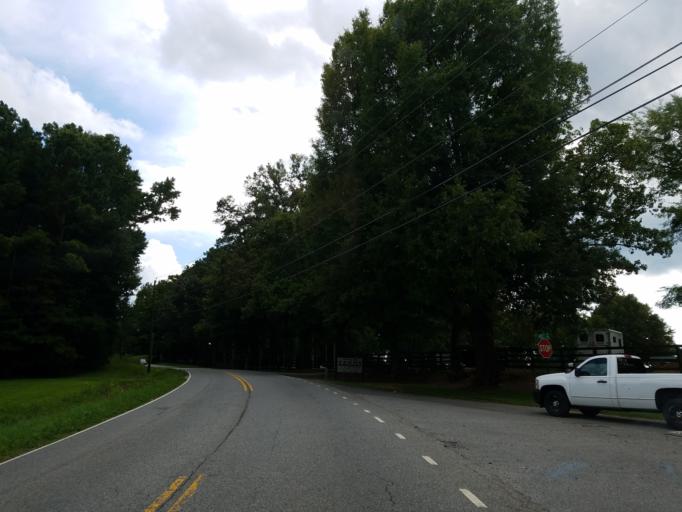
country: US
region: Georgia
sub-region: Bartow County
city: Cartersville
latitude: 34.2561
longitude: -84.8449
